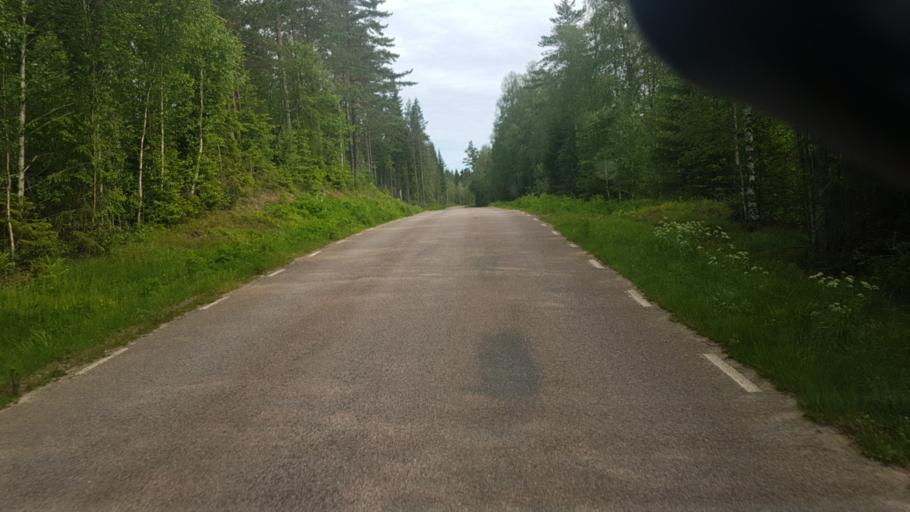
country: SE
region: Vaermland
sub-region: Arvika Kommun
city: Arvika
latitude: 59.8130
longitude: 12.8334
